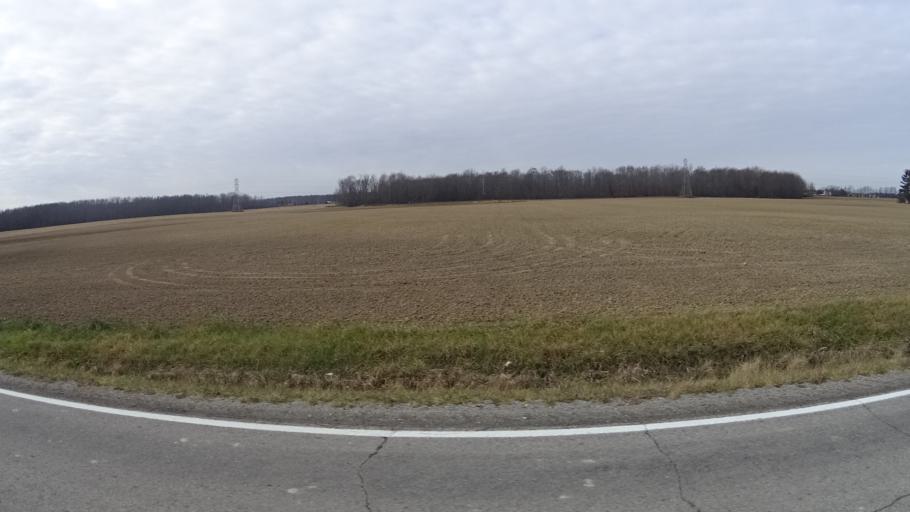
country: US
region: Ohio
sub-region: Lorain County
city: Camden
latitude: 41.1982
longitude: -82.2685
